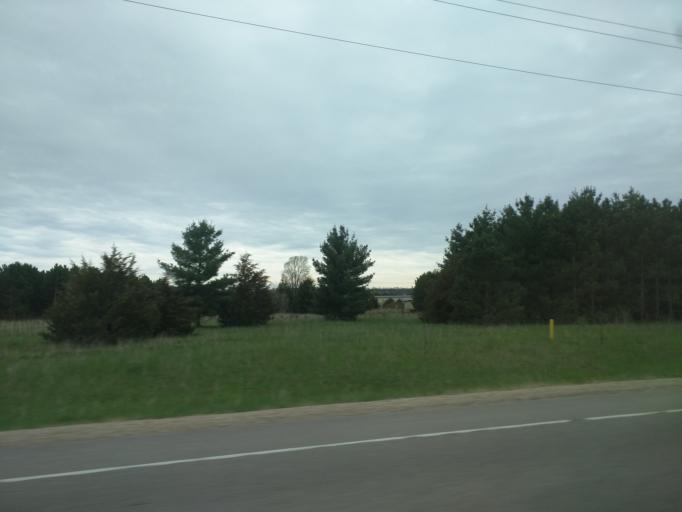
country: US
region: Minnesota
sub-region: Goodhue County
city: Red Wing
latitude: 44.5941
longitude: -92.5101
